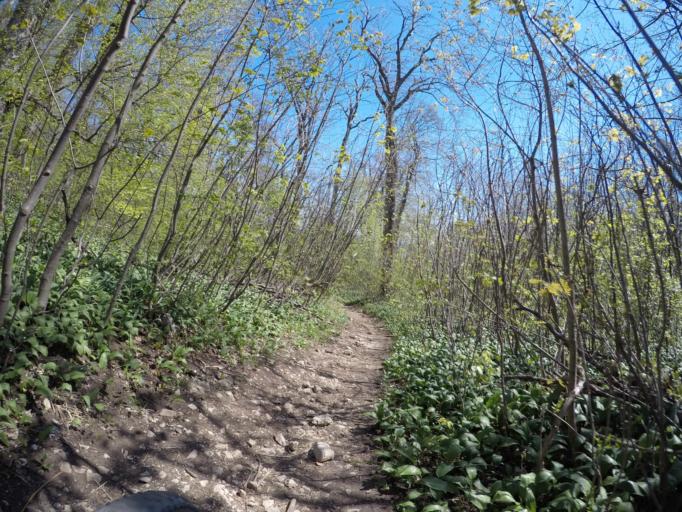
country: AT
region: Lower Austria
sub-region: Politischer Bezirk Modling
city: Gumpoldskirchen
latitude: 48.0510
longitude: 16.2526
